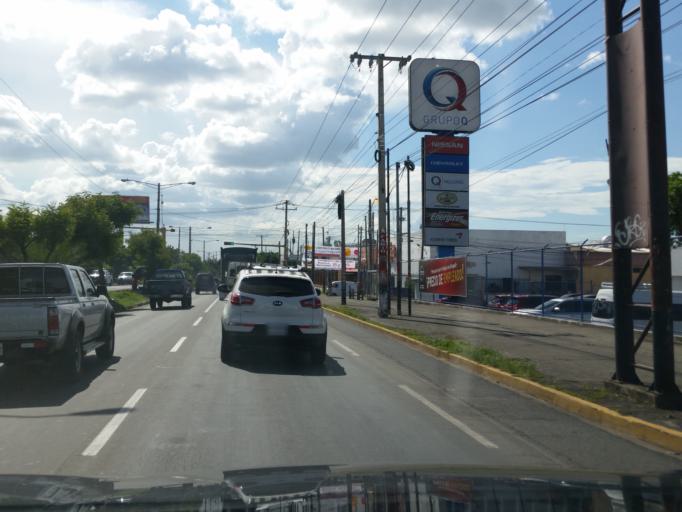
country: NI
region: Managua
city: Managua
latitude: 12.1515
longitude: -86.2322
